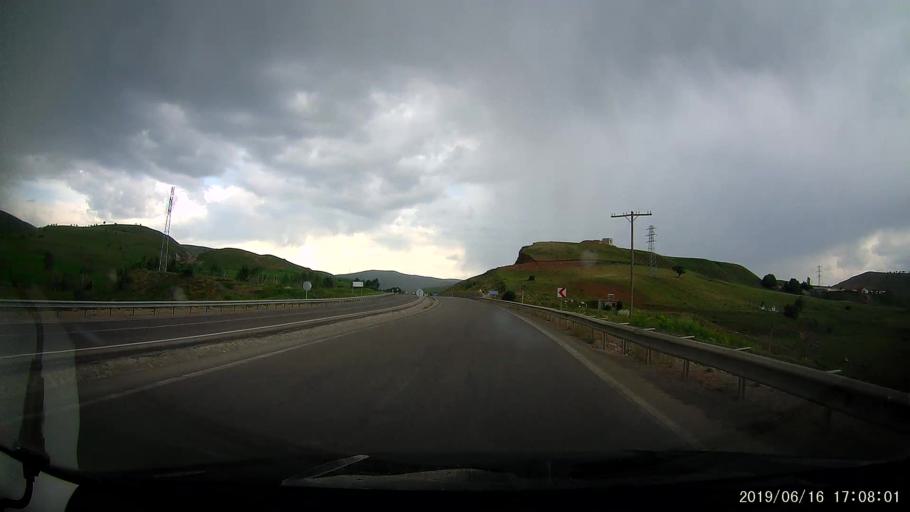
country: TR
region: Erzurum
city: Askale
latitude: 39.9144
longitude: 40.6660
